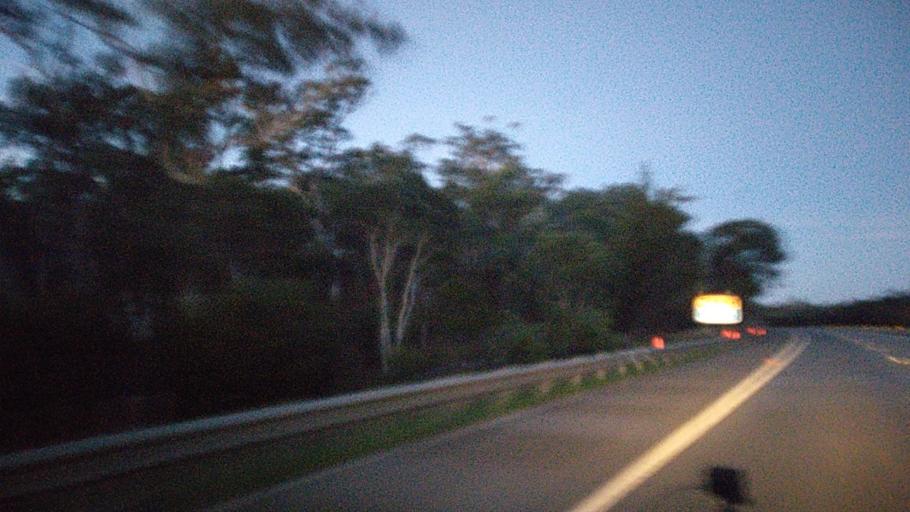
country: AU
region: New South Wales
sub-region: Wingecarribee
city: Moss Vale
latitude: -34.4790
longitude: 150.3170
